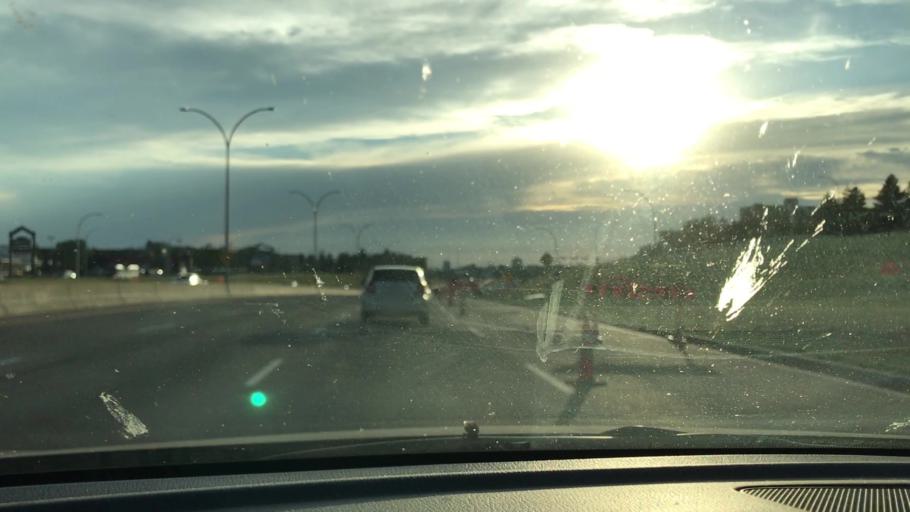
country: CA
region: Alberta
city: Edmonton
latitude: 53.4807
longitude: -113.4964
